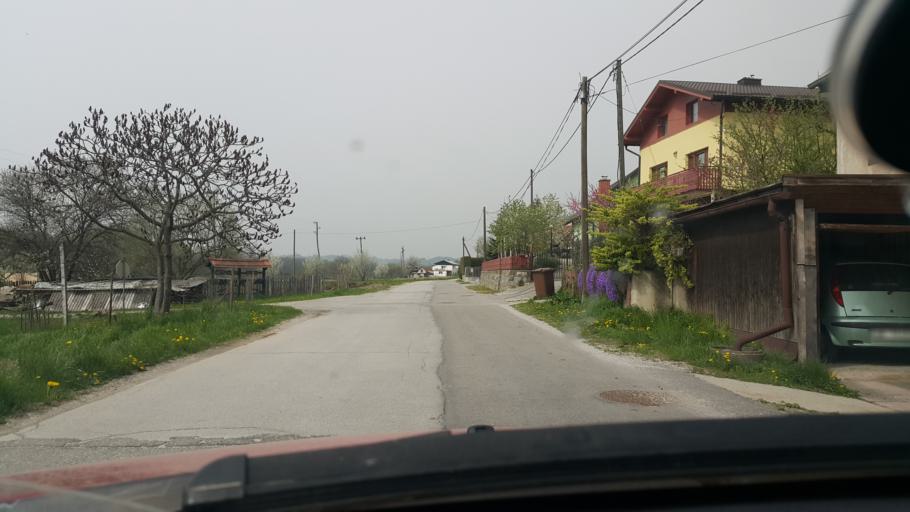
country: SI
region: Duplek
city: Zgornji Duplek
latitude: 46.5194
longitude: 15.7168
